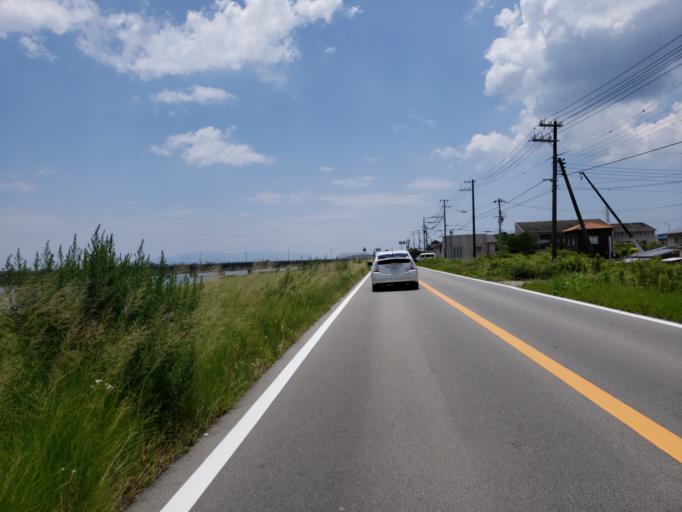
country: JP
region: Hyogo
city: Kariya
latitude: 34.7522
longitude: 134.4009
